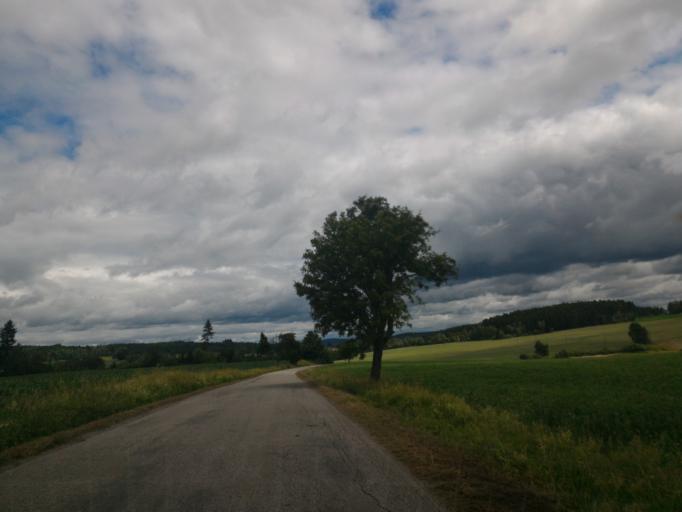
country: CZ
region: Vysocina
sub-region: Okres Jihlava
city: Telc
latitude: 49.2281
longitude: 15.4240
